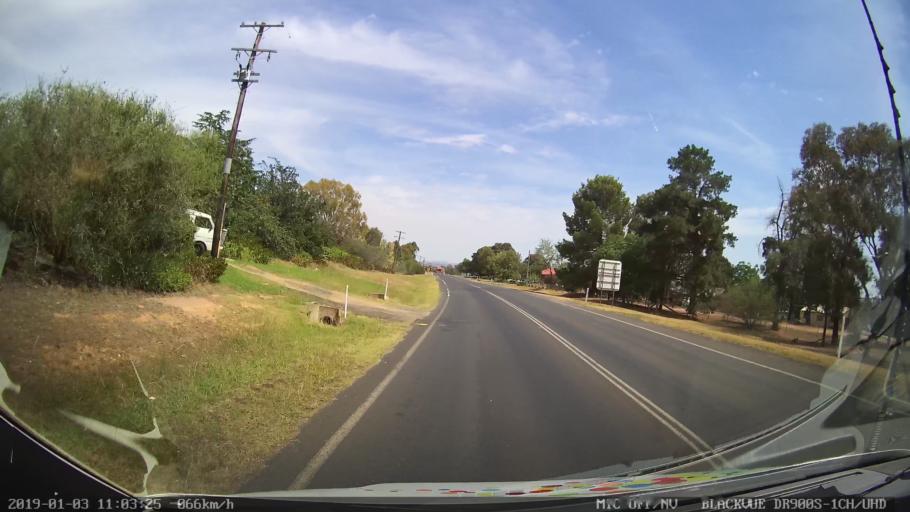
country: AU
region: New South Wales
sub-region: Young
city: Young
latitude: -34.2906
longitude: 148.2949
